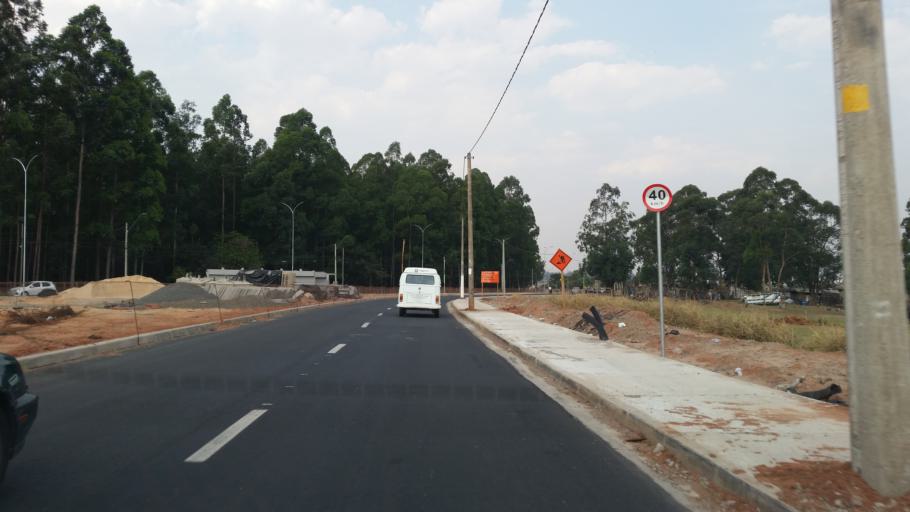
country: BR
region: Sao Paulo
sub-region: Hortolandia
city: Hortolandia
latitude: -22.9429
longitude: -47.1790
